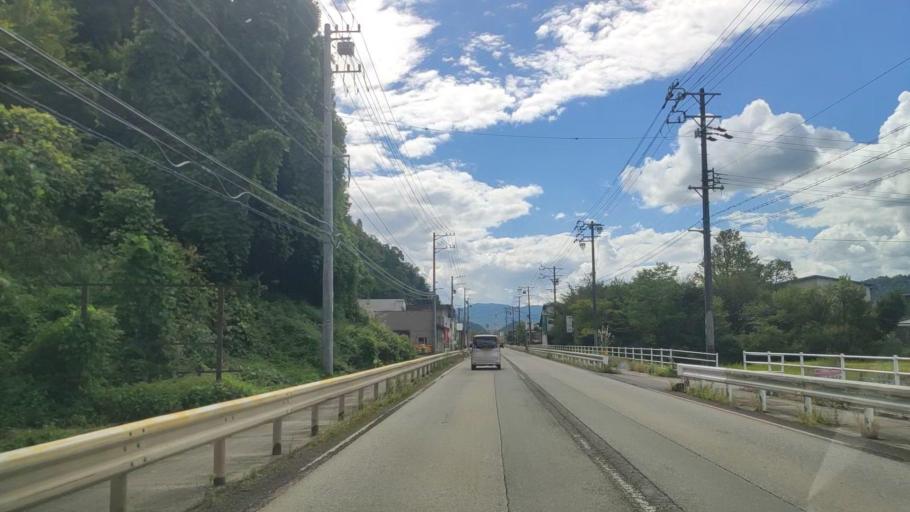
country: JP
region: Gifu
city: Takayama
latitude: 36.1820
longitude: 137.2516
